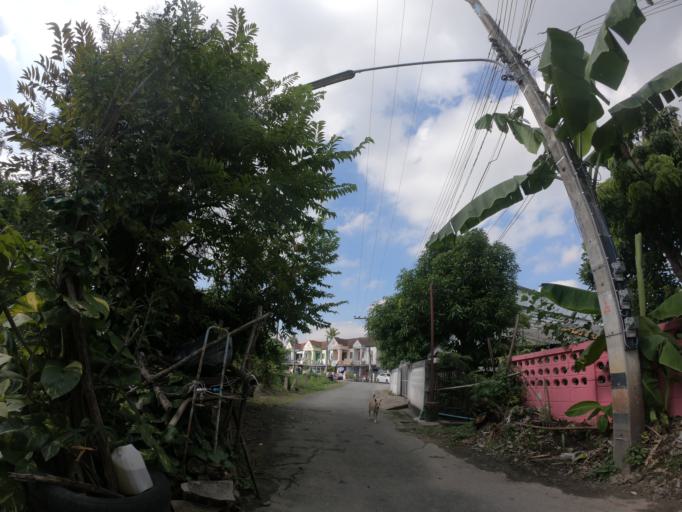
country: TH
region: Chiang Mai
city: Chiang Mai
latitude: 18.7852
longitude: 99.0337
